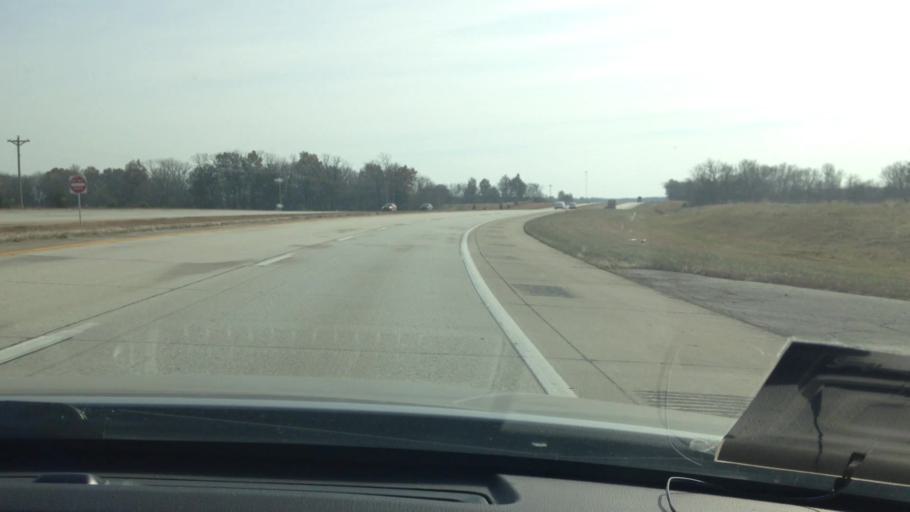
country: US
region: Missouri
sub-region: Henry County
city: Clinton
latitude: 38.4624
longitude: -93.9702
